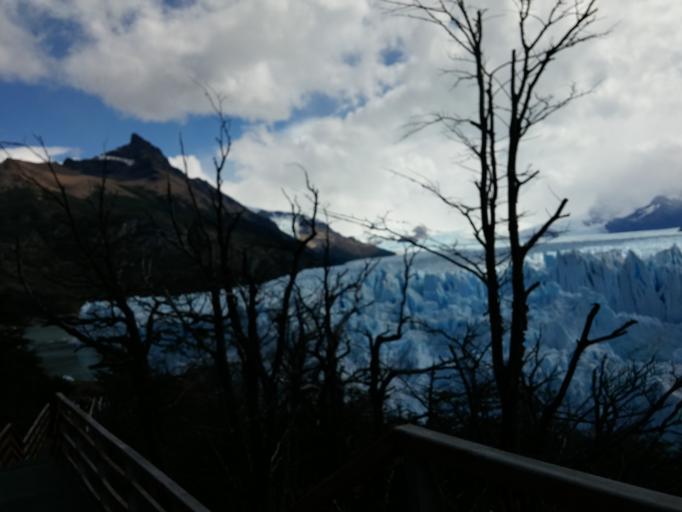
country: AR
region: Santa Cruz
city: El Calafate
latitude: -50.4711
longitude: -73.0329
